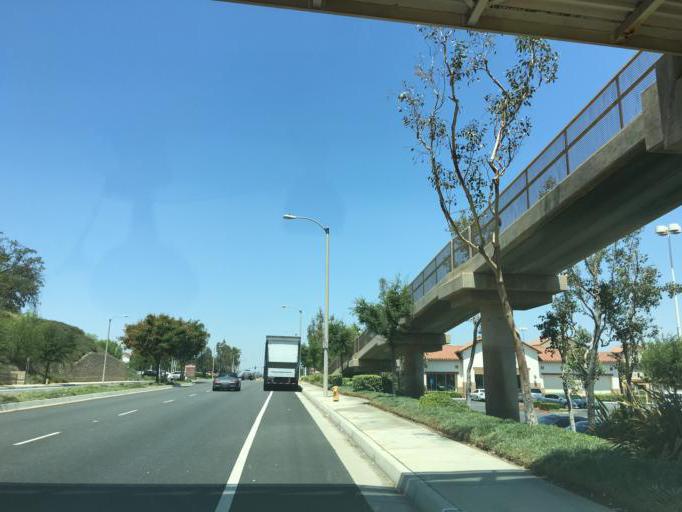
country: US
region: California
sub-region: Los Angeles County
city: Santa Clarita
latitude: 34.3907
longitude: -118.5734
